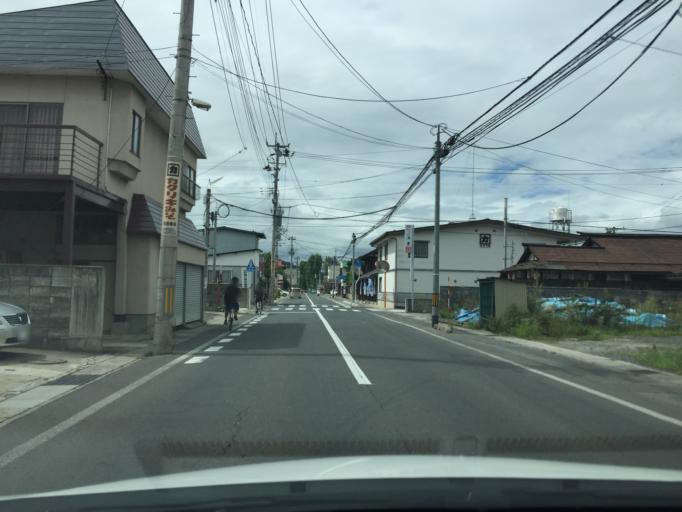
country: JP
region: Yamagata
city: Yonezawa
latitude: 37.9029
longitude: 140.1137
